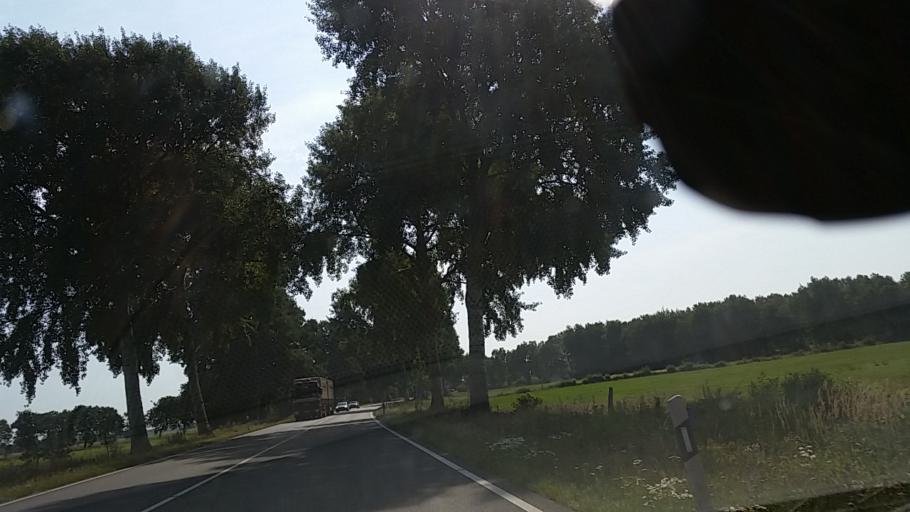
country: DE
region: Lower Saxony
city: Diepholz
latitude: 52.6138
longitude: 8.3120
